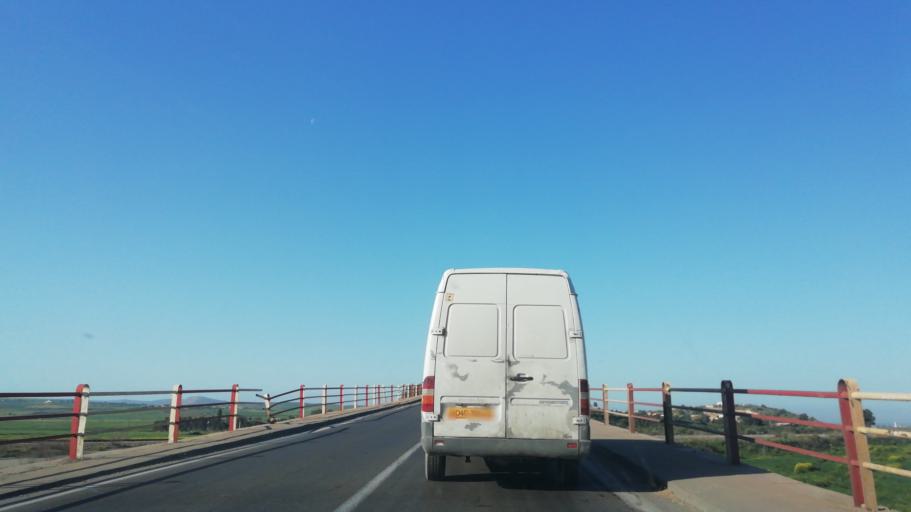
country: DZ
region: Mascara
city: Mascara
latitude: 35.6512
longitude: 0.1838
